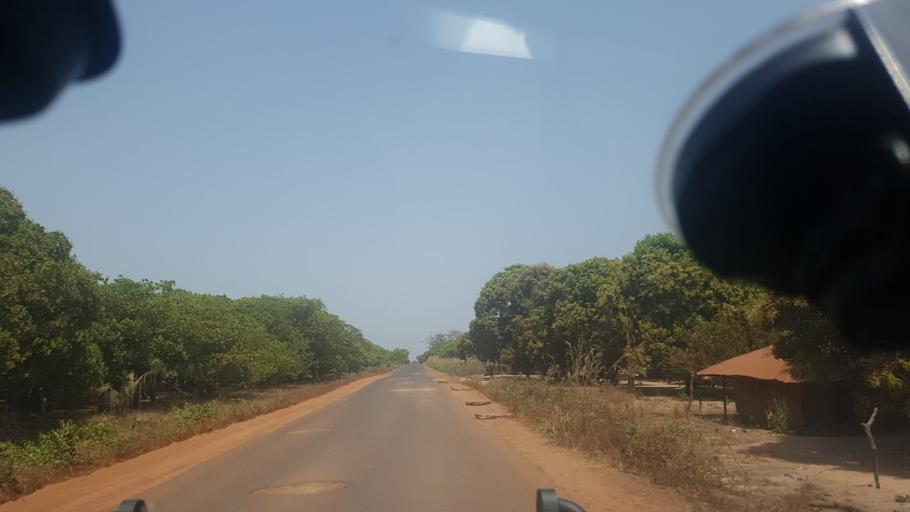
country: GW
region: Oio
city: Bissora
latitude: 12.3014
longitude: -15.7645
